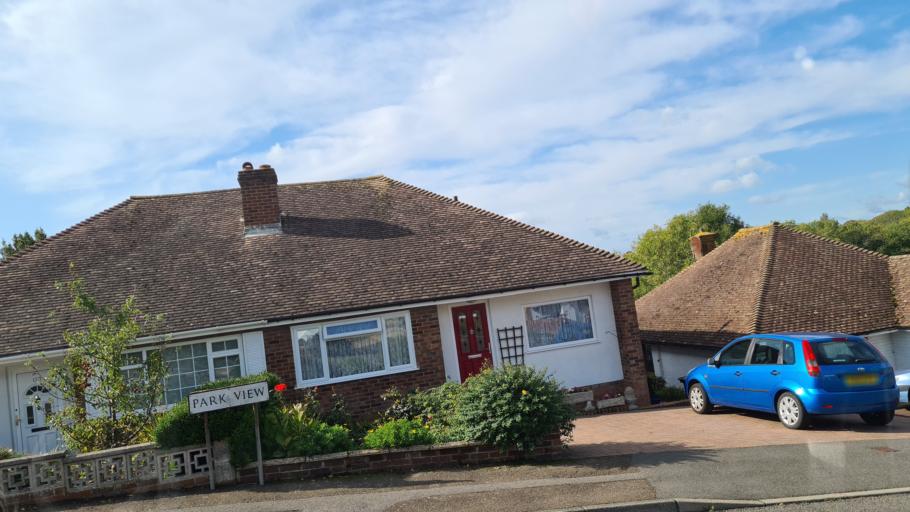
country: GB
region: England
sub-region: East Sussex
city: Hastings
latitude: 50.8722
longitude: 0.5676
